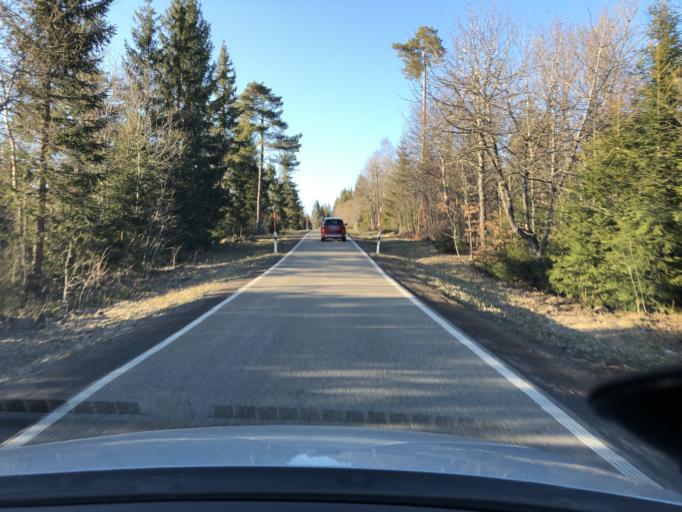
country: DE
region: Baden-Wuerttemberg
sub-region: Freiburg Region
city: Schluchsee
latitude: 47.8248
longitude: 8.2092
